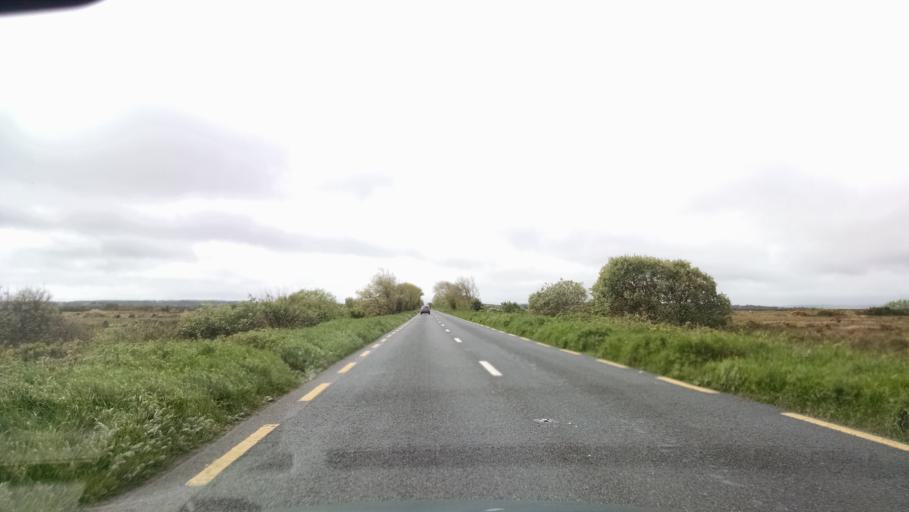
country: IE
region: Connaught
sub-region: County Galway
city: Claregalway
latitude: 53.3578
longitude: -9.0177
